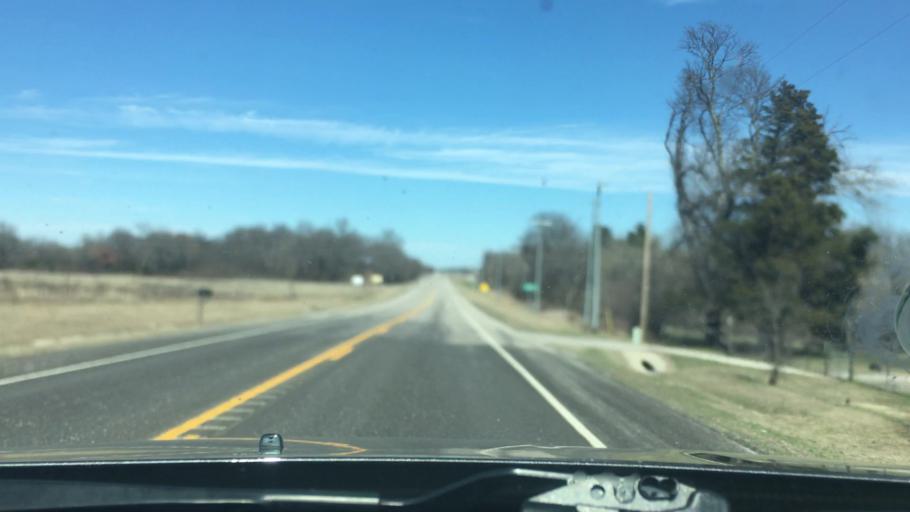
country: US
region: Oklahoma
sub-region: Murray County
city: Sulphur
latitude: 34.3592
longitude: -96.9509
